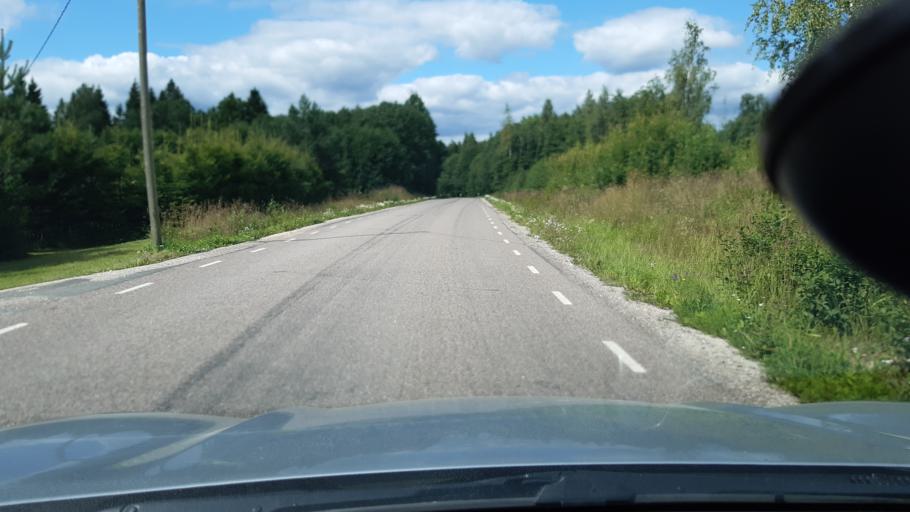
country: EE
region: Raplamaa
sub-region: Jaervakandi vald
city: Jarvakandi
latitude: 58.7989
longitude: 24.9035
